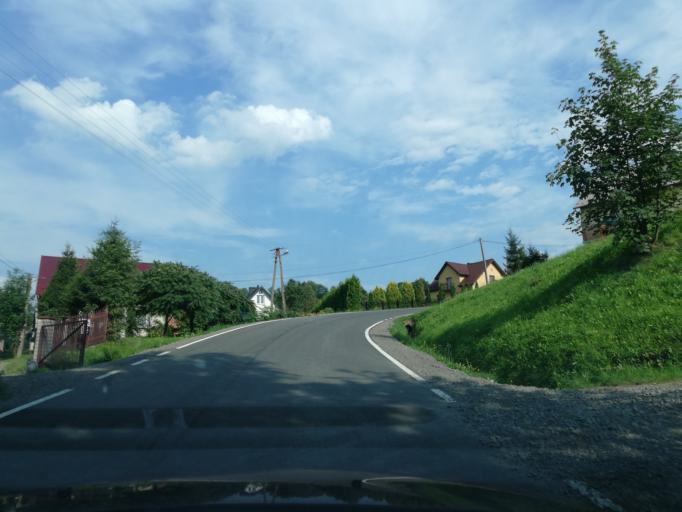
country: PL
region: Lesser Poland Voivodeship
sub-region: Powiat nowosadecki
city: Nawojowa
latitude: 49.5383
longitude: 20.7403
